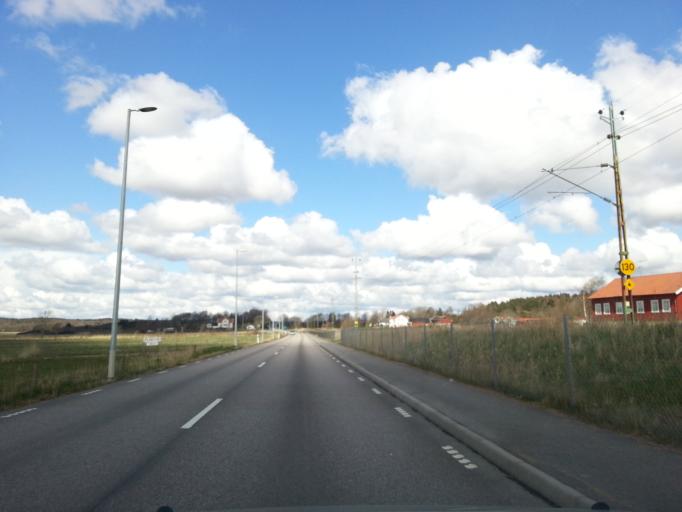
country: SE
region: Vaestra Goetaland
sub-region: Kungalvs Kommun
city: Kungalv
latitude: 57.8079
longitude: 11.9090
